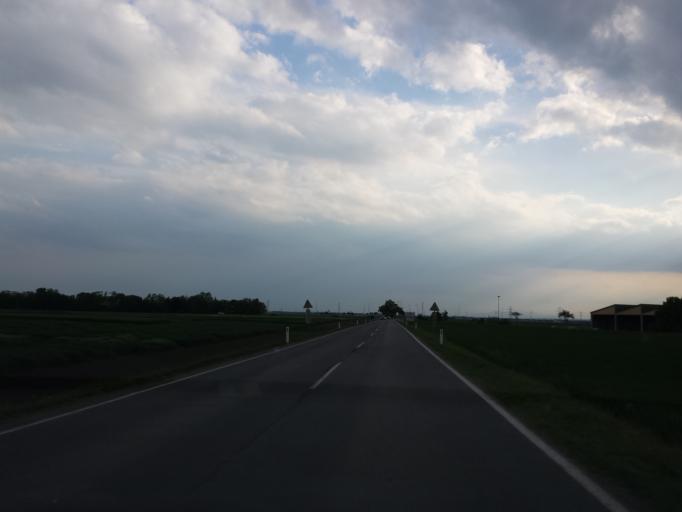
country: AT
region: Lower Austria
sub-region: Politischer Bezirk Ganserndorf
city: Raasdorf
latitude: 48.2381
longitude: 16.5887
